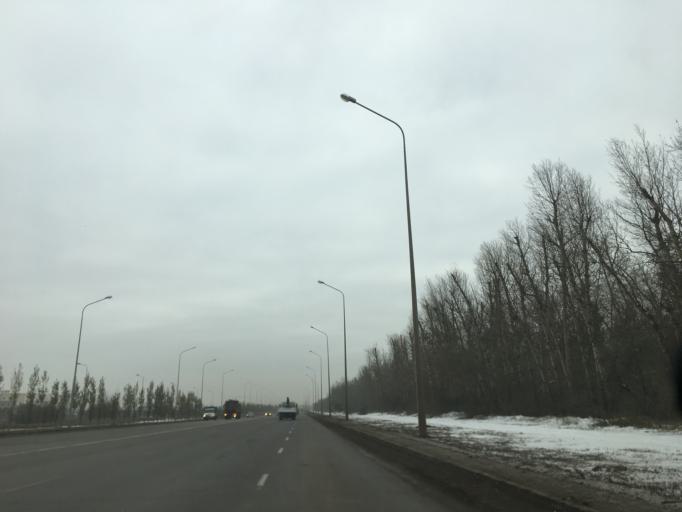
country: KZ
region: Astana Qalasy
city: Astana
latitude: 51.1666
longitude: 71.5020
